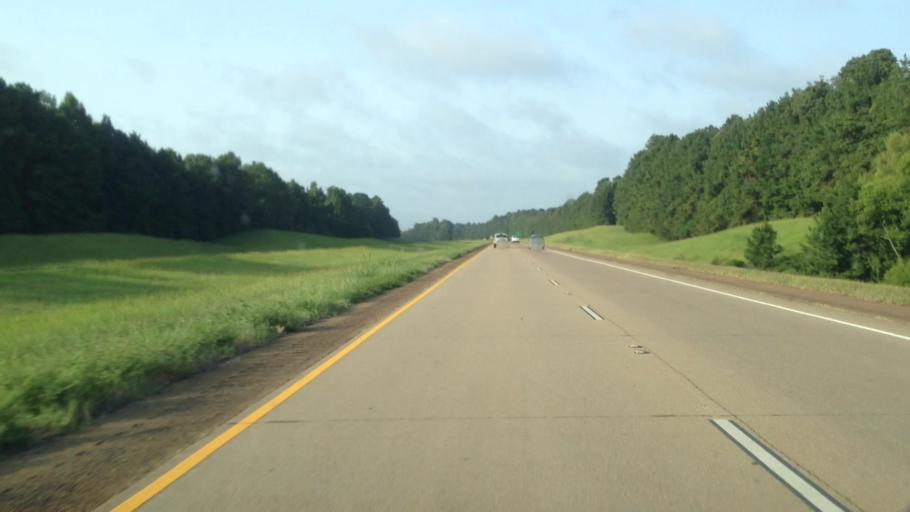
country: US
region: Louisiana
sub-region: Rapides Parish
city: Lecompte
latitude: 31.1094
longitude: -92.4443
